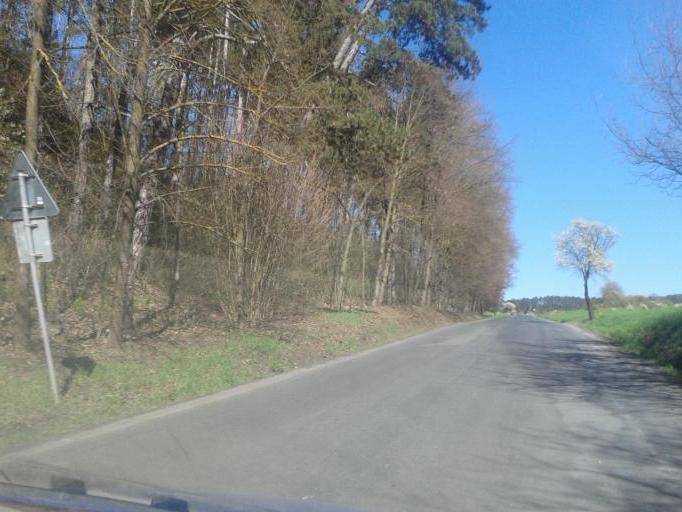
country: CZ
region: Central Bohemia
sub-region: Okres Beroun
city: Kraluv Dvur
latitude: 49.9293
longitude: 14.0500
